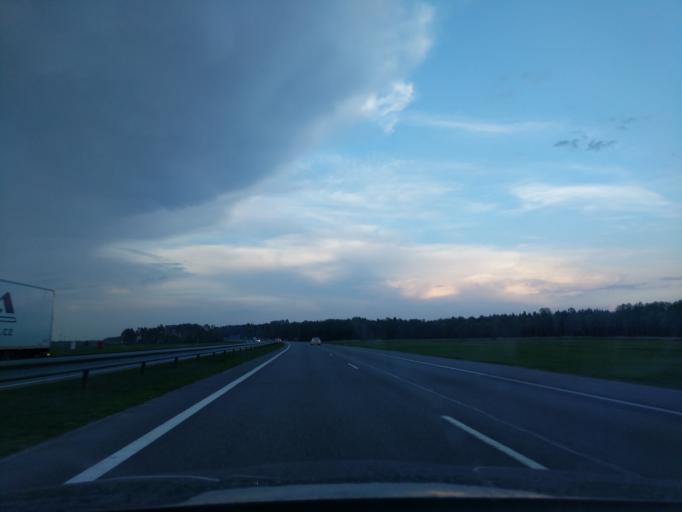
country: BY
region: Minsk
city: Dzyarzhynsk
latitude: 53.6605
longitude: 27.1270
